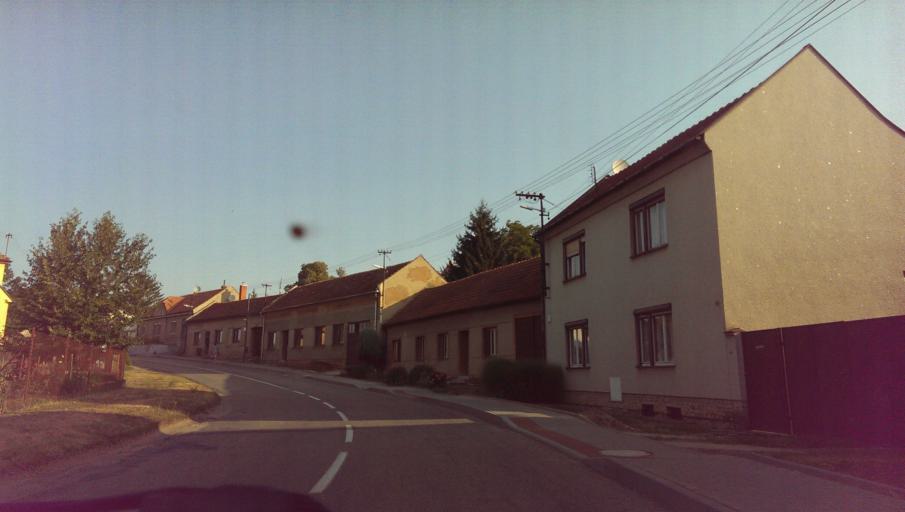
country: CZ
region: Zlin
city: Korycany
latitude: 49.1288
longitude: 17.1263
